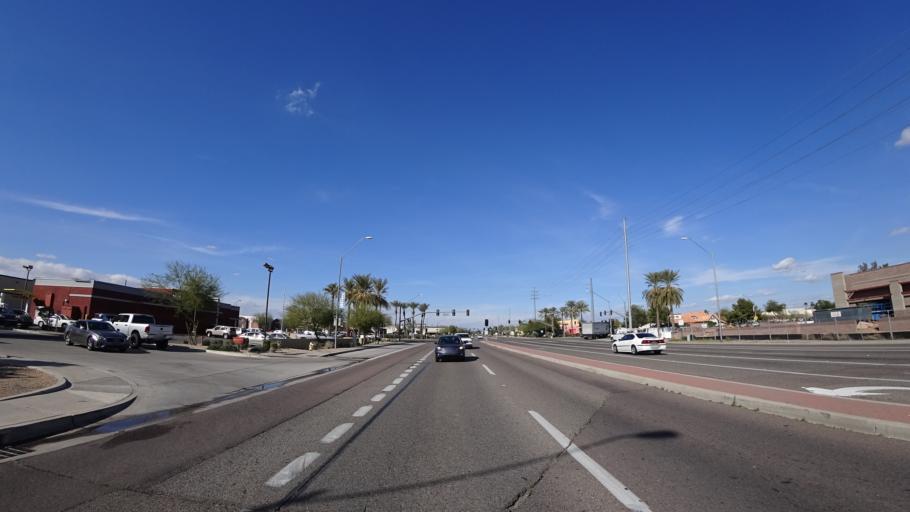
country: US
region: Arizona
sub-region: Maricopa County
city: Peoria
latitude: 33.6374
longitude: -112.2203
